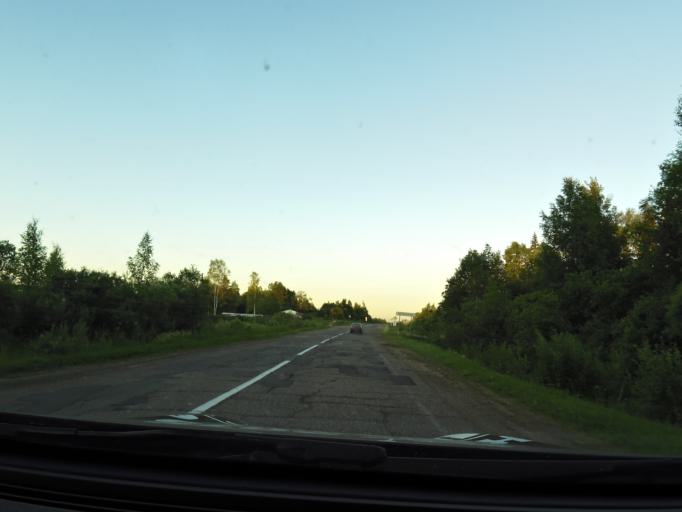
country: RU
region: Jaroslavl
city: Prechistoye
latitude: 58.3932
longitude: 40.4292
